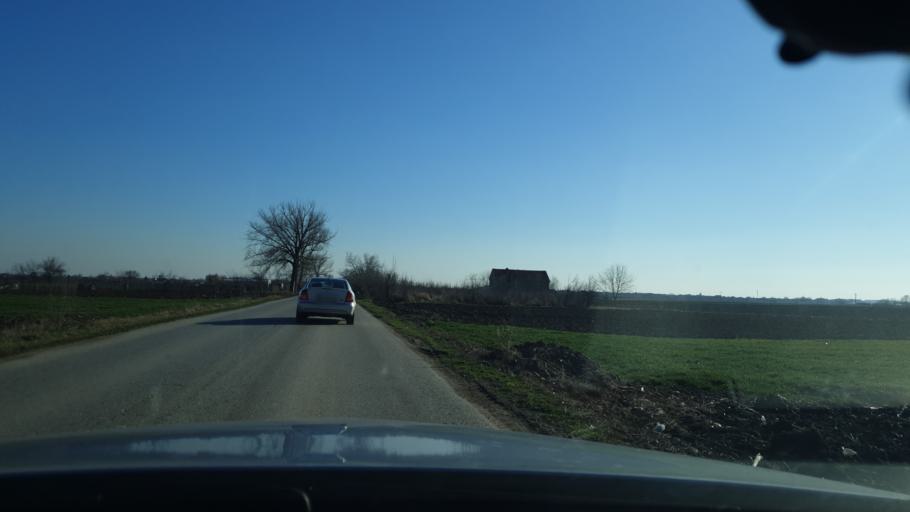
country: RS
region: Autonomna Pokrajina Vojvodina
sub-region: Sremski Okrug
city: Ruma
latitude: 45.0305
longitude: 19.8106
